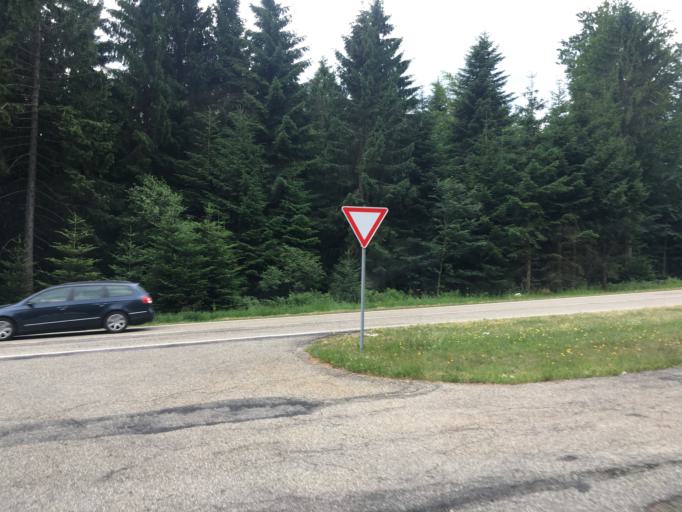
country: DE
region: Baden-Wuerttemberg
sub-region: Karlsruhe Region
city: Buhlertal
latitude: 48.6567
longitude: 8.2368
